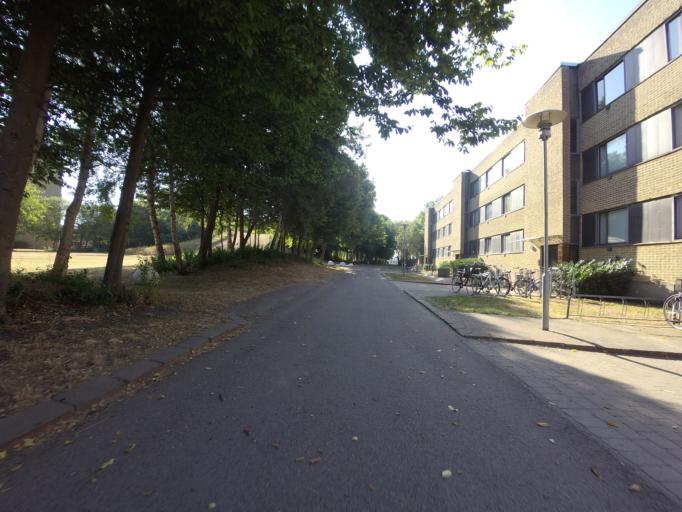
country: SE
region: Skane
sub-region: Landskrona
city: Landskrona
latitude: 55.8872
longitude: 12.8434
